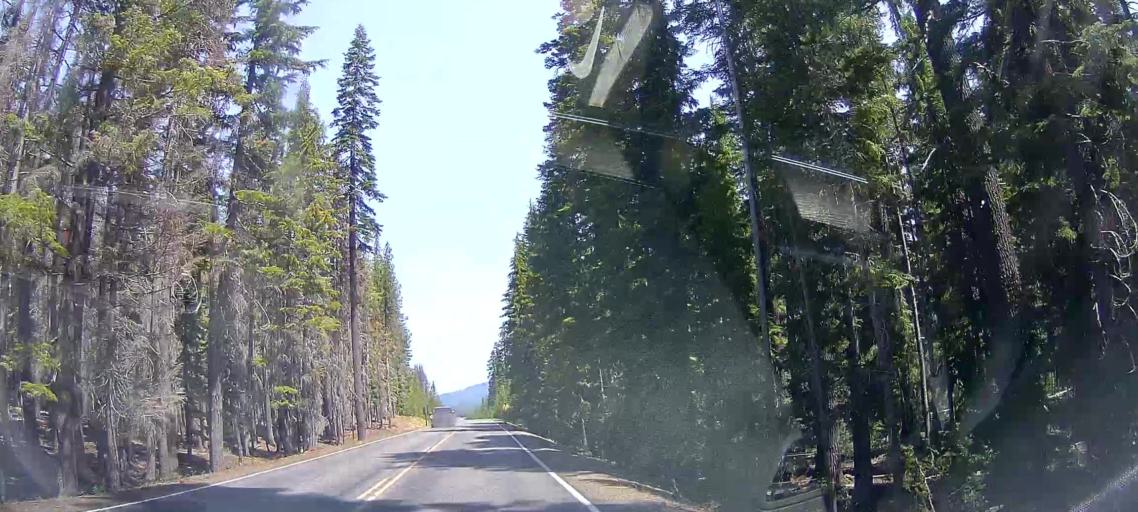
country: US
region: Oregon
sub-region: Lane County
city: Oakridge
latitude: 43.0665
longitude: -122.1199
